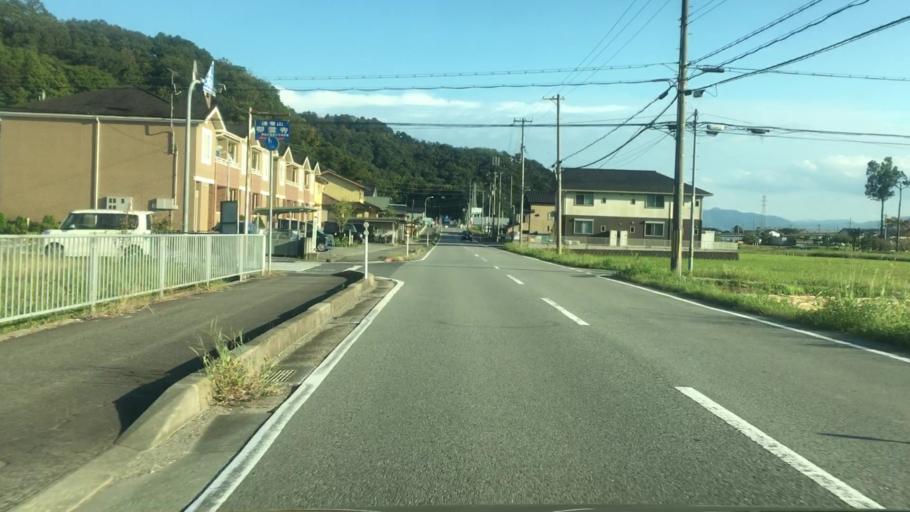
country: JP
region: Hyogo
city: Toyooka
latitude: 35.5624
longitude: 134.8216
